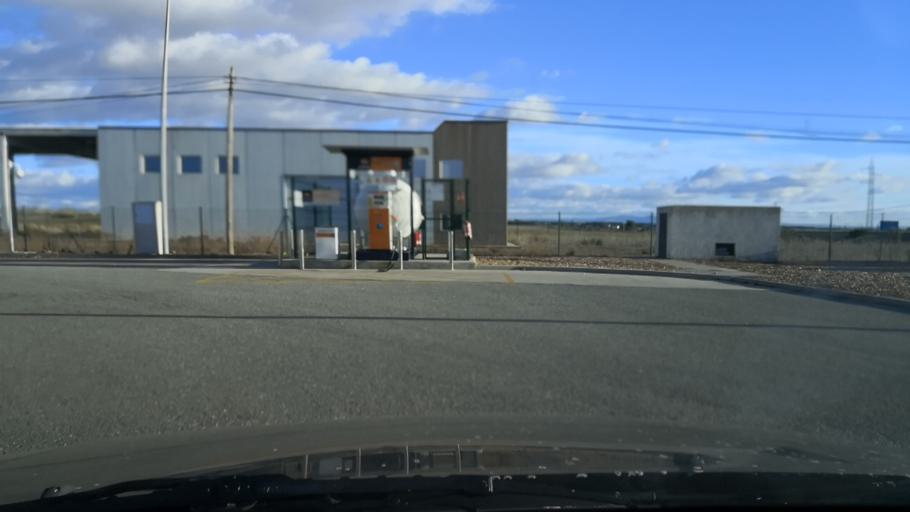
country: ES
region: Castille and Leon
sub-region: Provincia de Avila
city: Orbita
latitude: 41.0095
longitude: -4.6654
